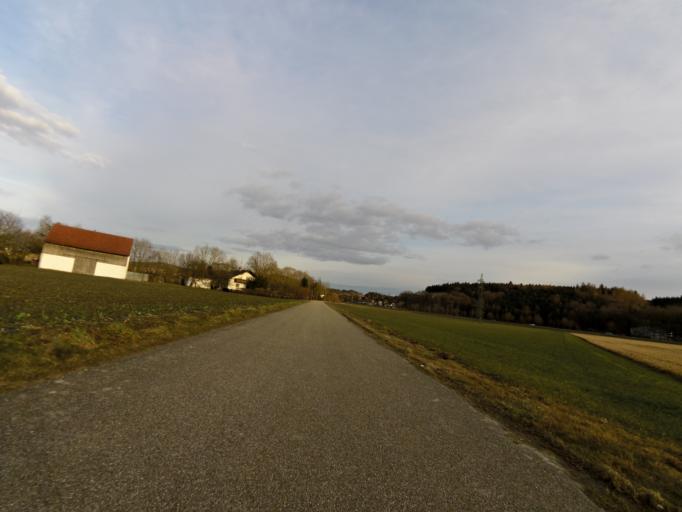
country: DE
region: Bavaria
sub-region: Lower Bavaria
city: Eching
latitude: 48.5003
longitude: 12.0494
